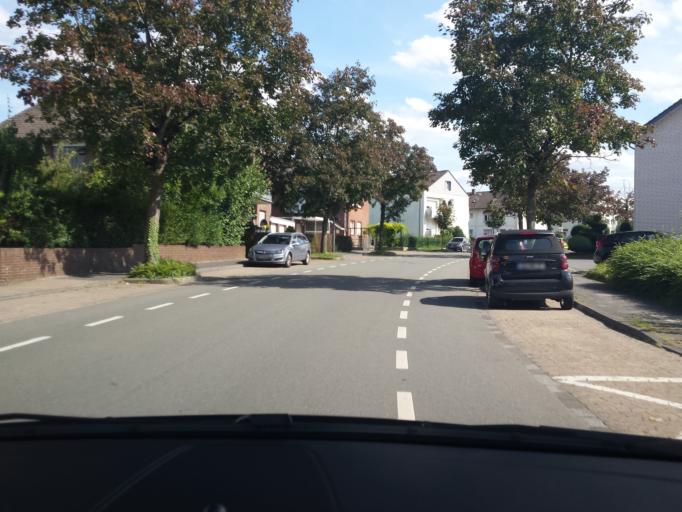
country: DE
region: North Rhine-Westphalia
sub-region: Regierungsbezirk Arnsberg
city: Lippstadt
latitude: 51.6617
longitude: 8.3278
